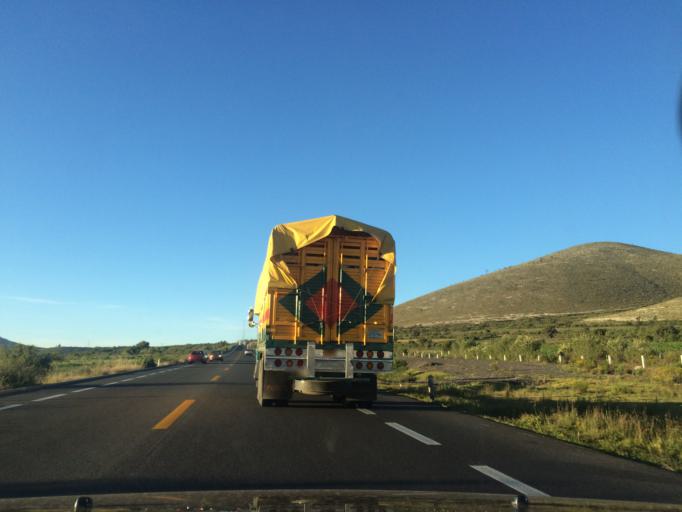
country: MX
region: Puebla
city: Morelos Canada
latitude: 18.7287
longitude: -97.4746
